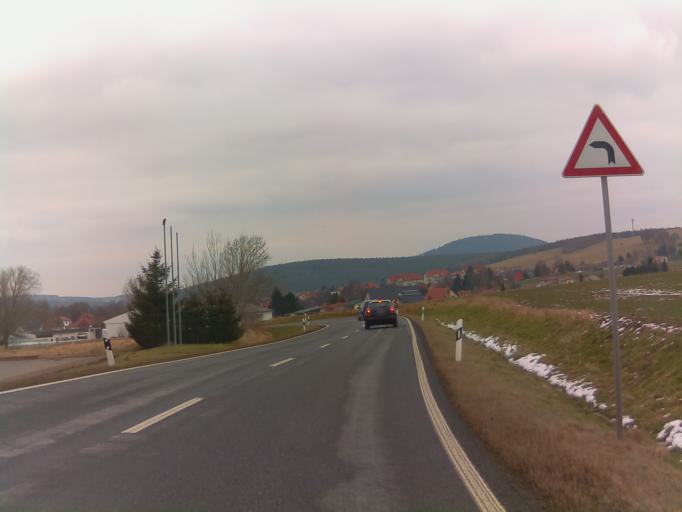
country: DE
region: Thuringia
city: Pennewitz
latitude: 50.6921
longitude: 11.0180
